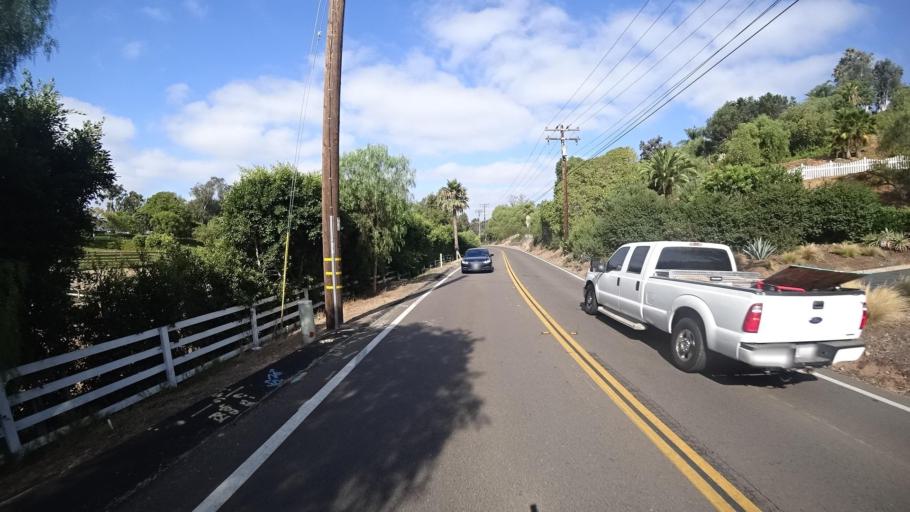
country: US
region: California
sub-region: San Diego County
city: Rancho Santa Fe
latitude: 33.0465
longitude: -117.2202
